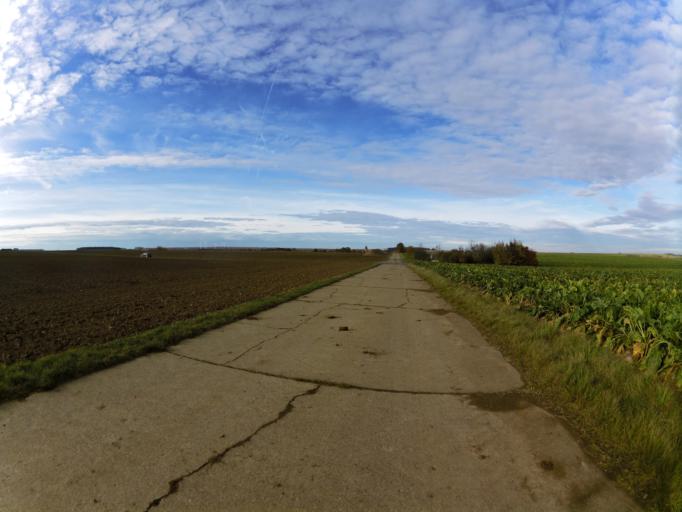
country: DE
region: Bavaria
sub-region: Regierungsbezirk Unterfranken
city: Giebelstadt
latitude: 49.6639
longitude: 9.9668
